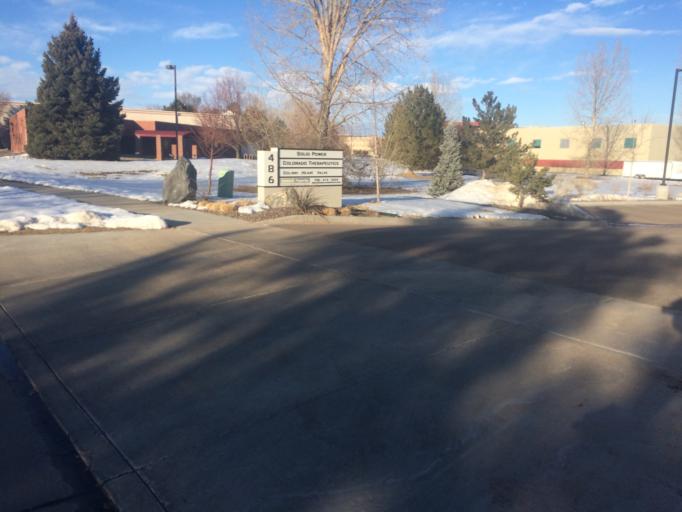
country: US
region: Colorado
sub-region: Boulder County
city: Louisville
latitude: 39.9638
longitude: -105.1221
